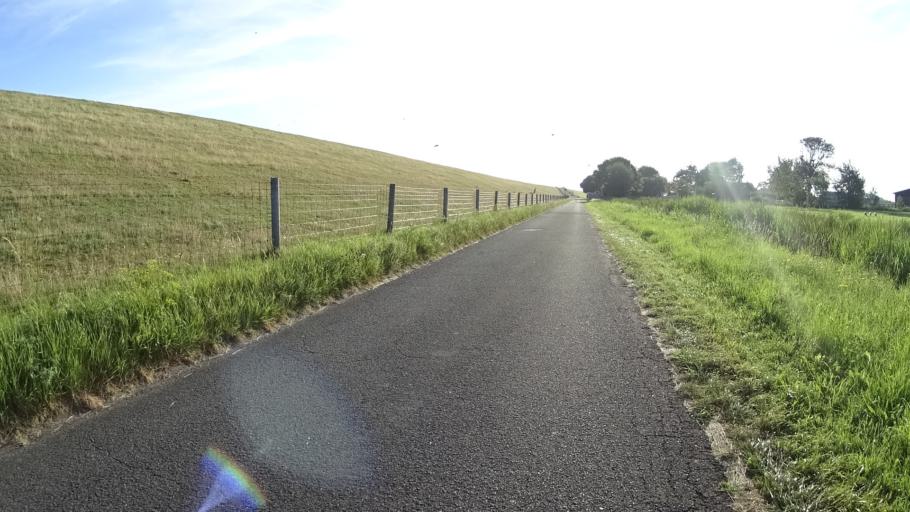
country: DE
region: Lower Saxony
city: Butjadingen
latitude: 53.6060
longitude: 8.2811
